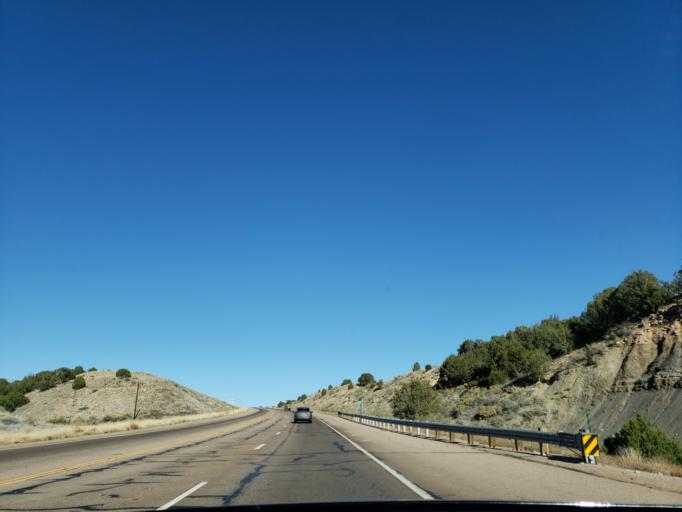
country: US
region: Colorado
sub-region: Fremont County
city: Penrose
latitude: 38.4696
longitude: -104.9887
